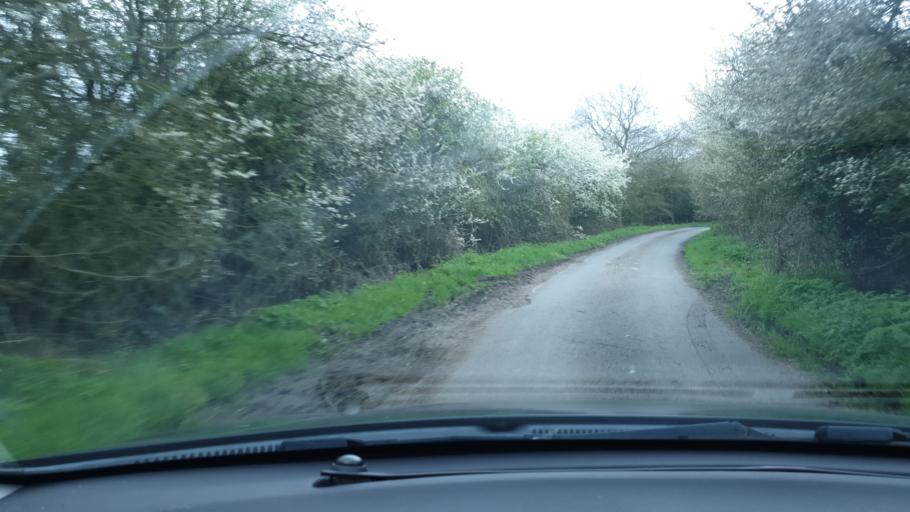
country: GB
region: England
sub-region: Essex
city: Little Clacton
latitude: 51.8916
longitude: 1.1308
